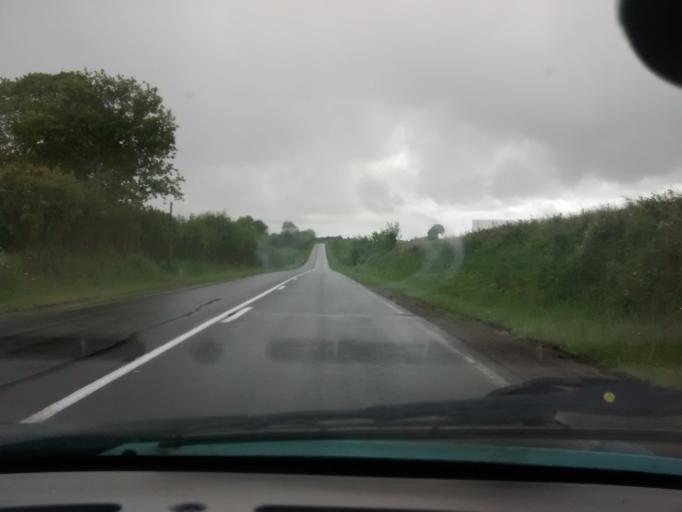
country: FR
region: Lower Normandy
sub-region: Departement de la Manche
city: Conde-sur-Vire
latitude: 49.0875
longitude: -1.0412
